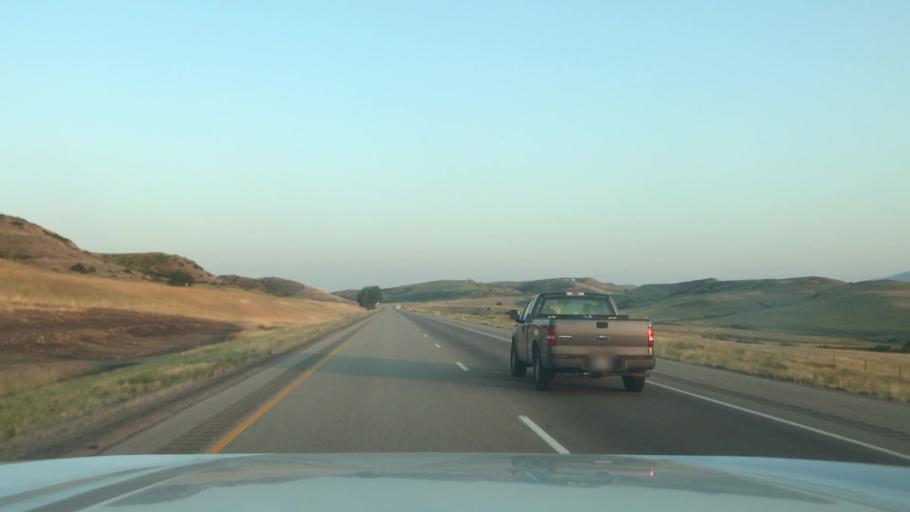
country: US
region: Wyoming
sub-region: Sheridan County
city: Sheridan
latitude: 44.7487
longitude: -106.9280
